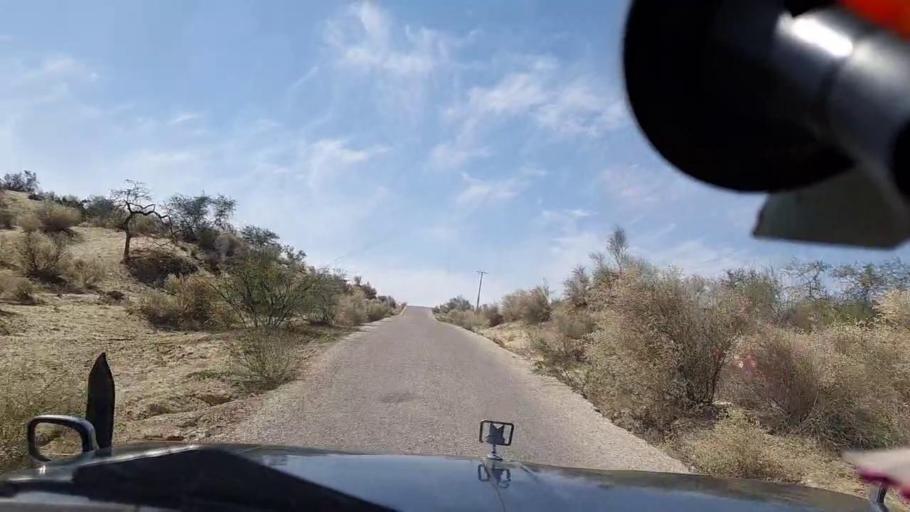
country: PK
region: Sindh
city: Diplo
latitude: 24.3840
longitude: 69.5866
